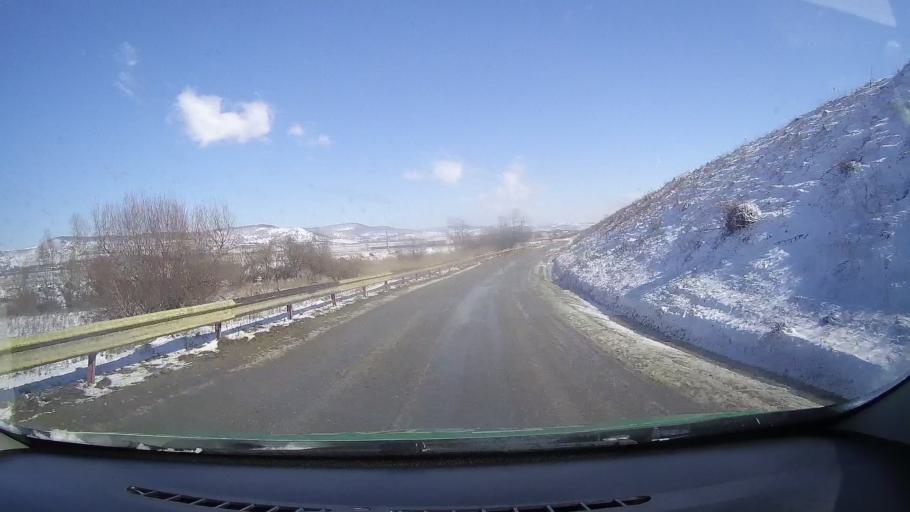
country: RO
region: Sibiu
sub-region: Comuna Avrig
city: Avrig
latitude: 45.7451
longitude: 24.3897
